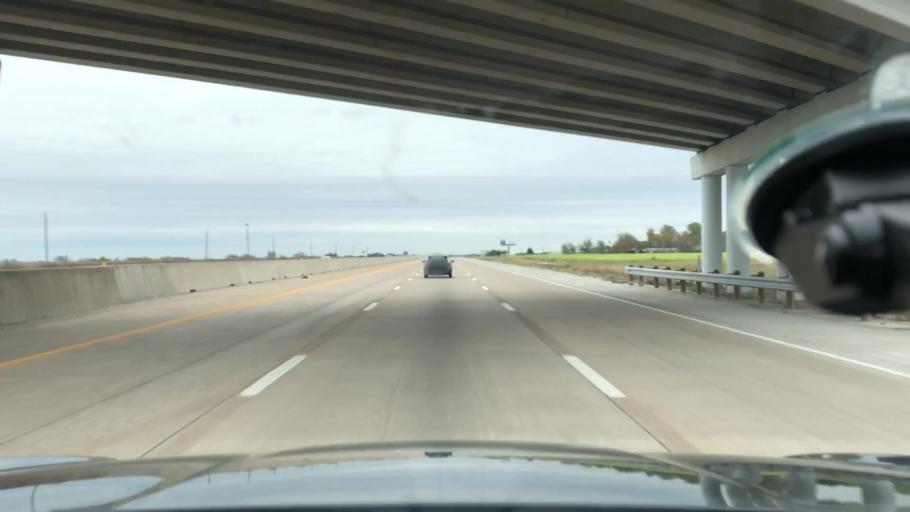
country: US
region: Texas
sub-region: Ellis County
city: Waxahachie
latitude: 32.3226
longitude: -96.8600
